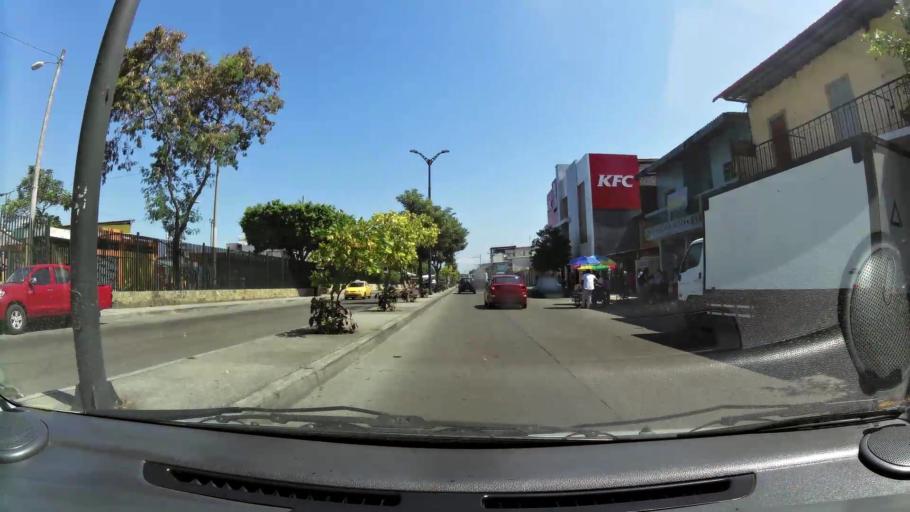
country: EC
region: Guayas
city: Guayaquil
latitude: -2.2096
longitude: -79.9294
